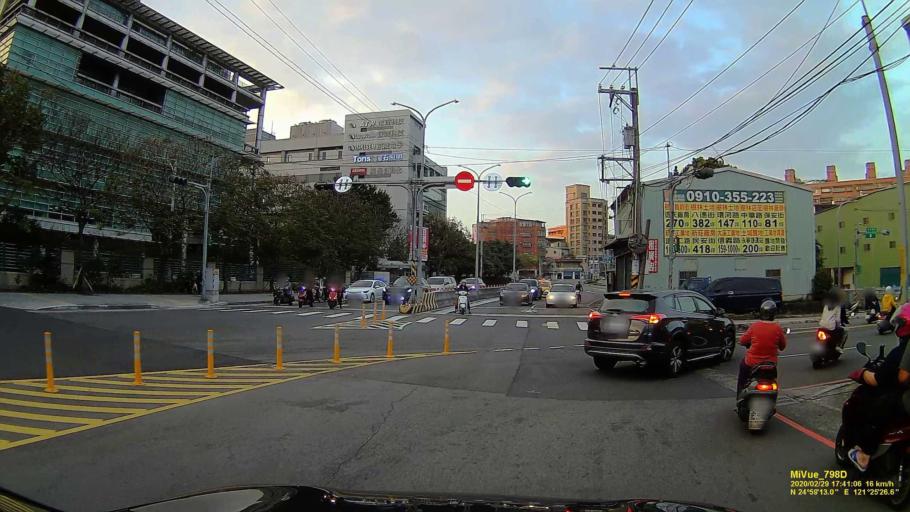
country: TW
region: Taipei
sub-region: Taipei
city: Banqiao
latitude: 24.9870
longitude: 121.4241
